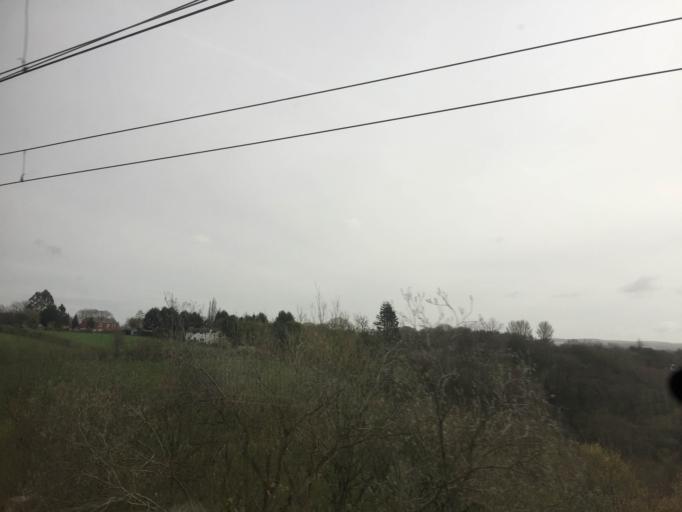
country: GB
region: England
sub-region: Lancashire
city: Coppull
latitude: 53.6323
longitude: -2.6628
